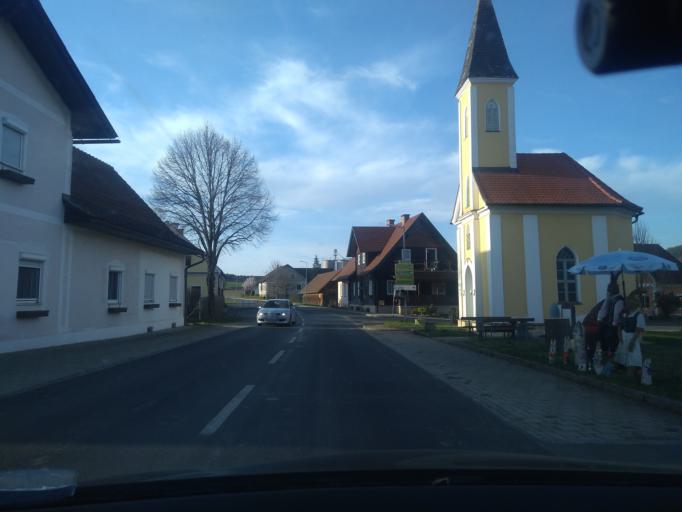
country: AT
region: Styria
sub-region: Politischer Bezirk Suedoststeiermark
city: Sankt Peter am Ottersbach
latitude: 46.8248
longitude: 15.7558
